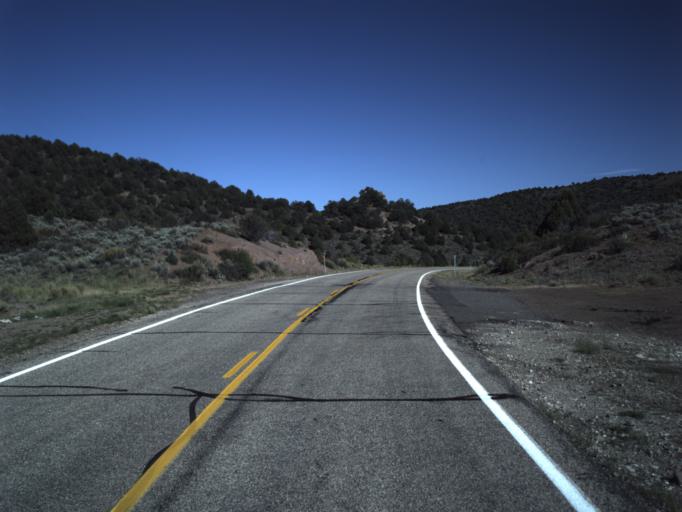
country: US
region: Utah
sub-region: Garfield County
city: Panguitch
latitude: 37.7626
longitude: -112.5193
